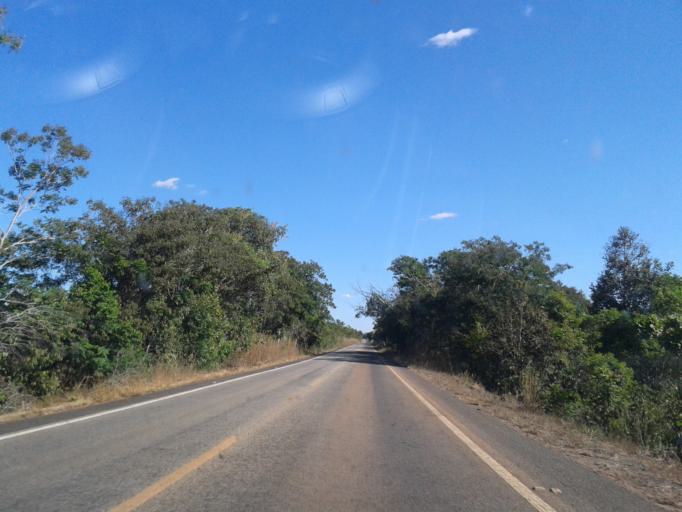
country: BR
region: Goias
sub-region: Mozarlandia
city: Mozarlandia
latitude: -14.6075
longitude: -50.5140
